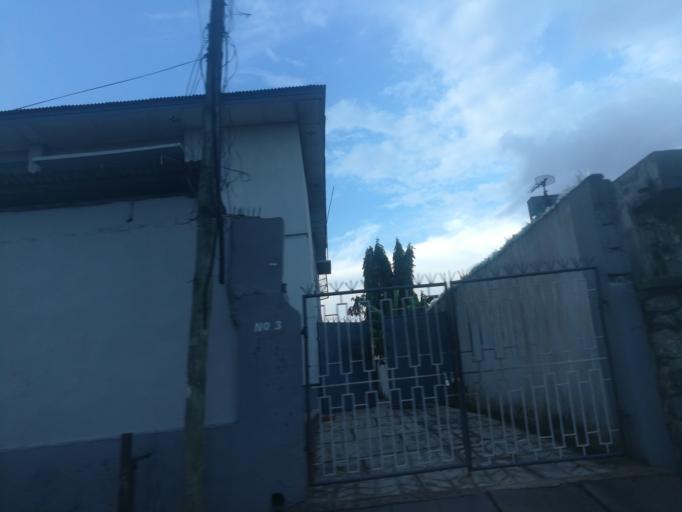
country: NG
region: Lagos
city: Somolu
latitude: 6.5607
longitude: 3.3719
